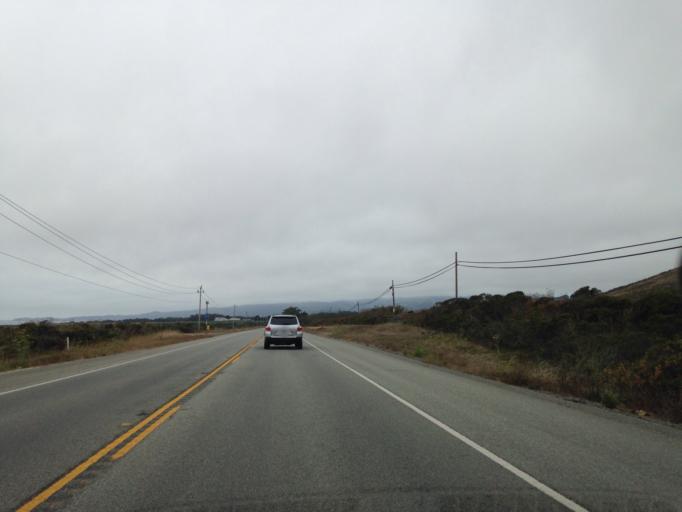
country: US
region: California
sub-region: San Mateo County
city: Half Moon Bay
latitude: 37.4103
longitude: -122.4221
